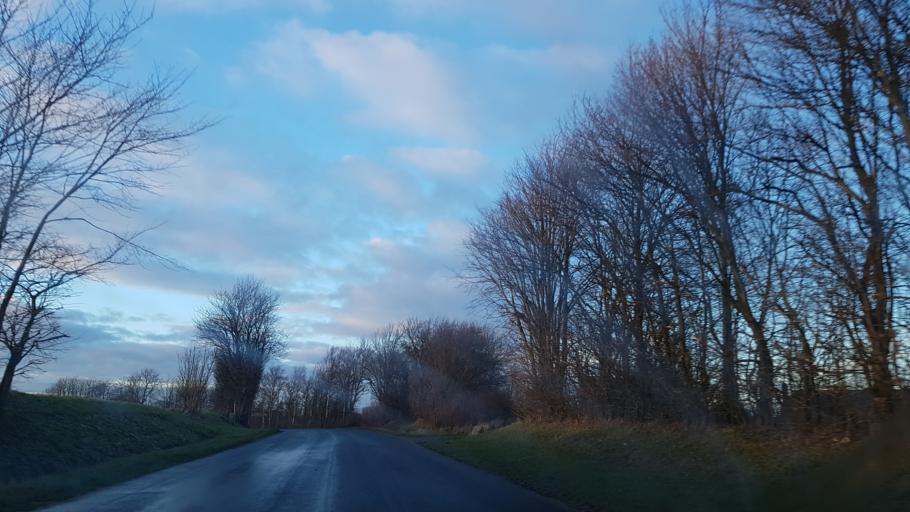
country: DK
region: South Denmark
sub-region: Kolding Kommune
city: Vamdrup
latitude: 55.3718
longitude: 9.3064
